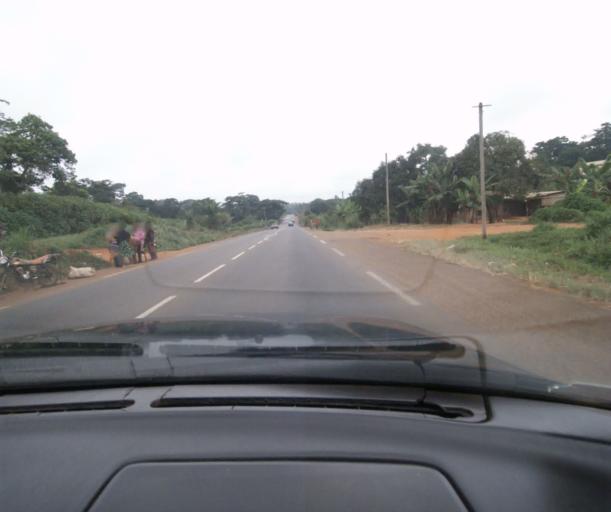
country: CM
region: Centre
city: Obala
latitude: 4.0787
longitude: 11.5510
